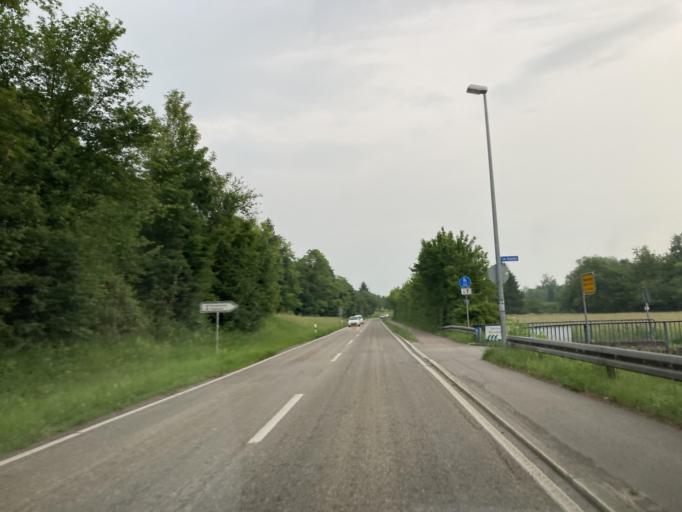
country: DE
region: Baden-Wuerttemberg
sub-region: Karlsruhe Region
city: Weingarten
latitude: 49.0824
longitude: 8.5634
